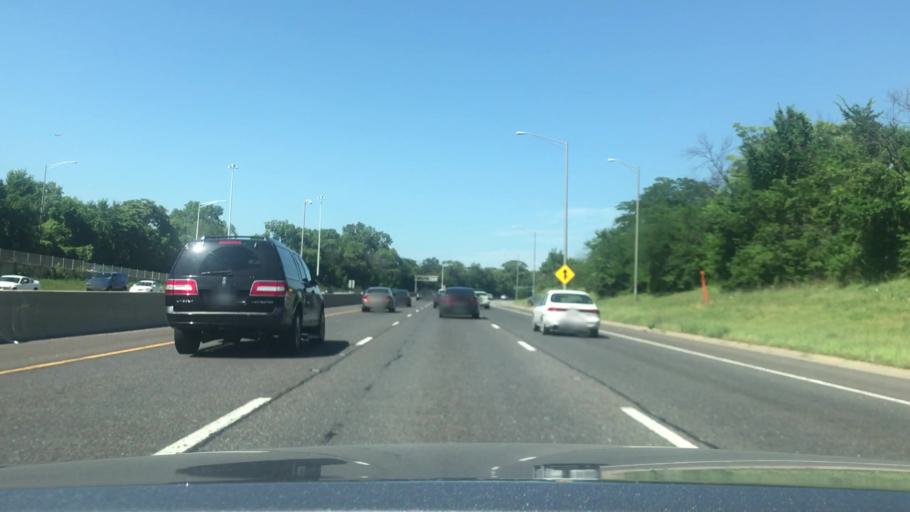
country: US
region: Illinois
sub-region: Cook County
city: Calumet Park
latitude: 41.6935
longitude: -87.6596
